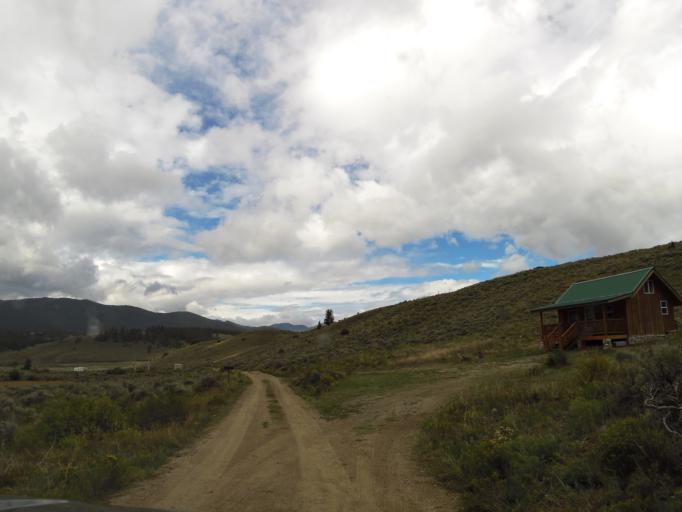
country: US
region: Colorado
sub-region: Chaffee County
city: Salida
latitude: 38.4094
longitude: -106.0594
